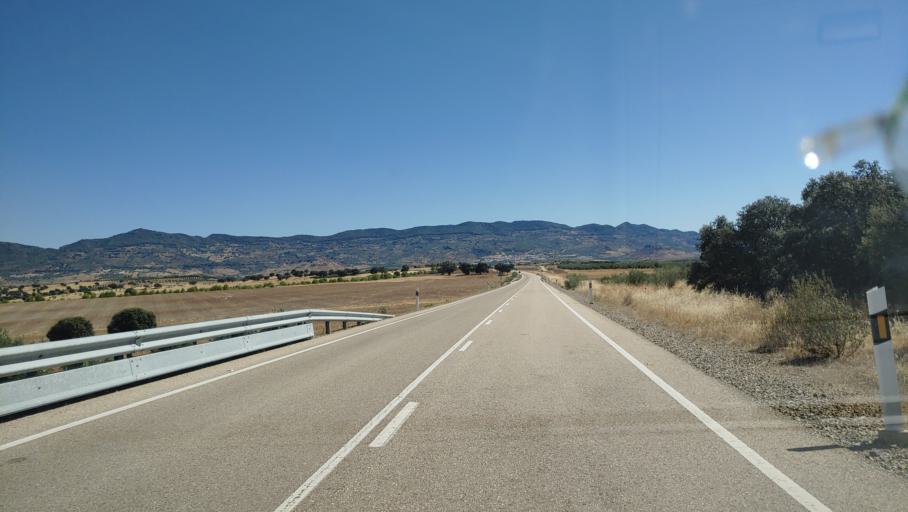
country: ES
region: Andalusia
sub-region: Provincia de Jaen
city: Genave
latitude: 38.4784
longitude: -2.7606
